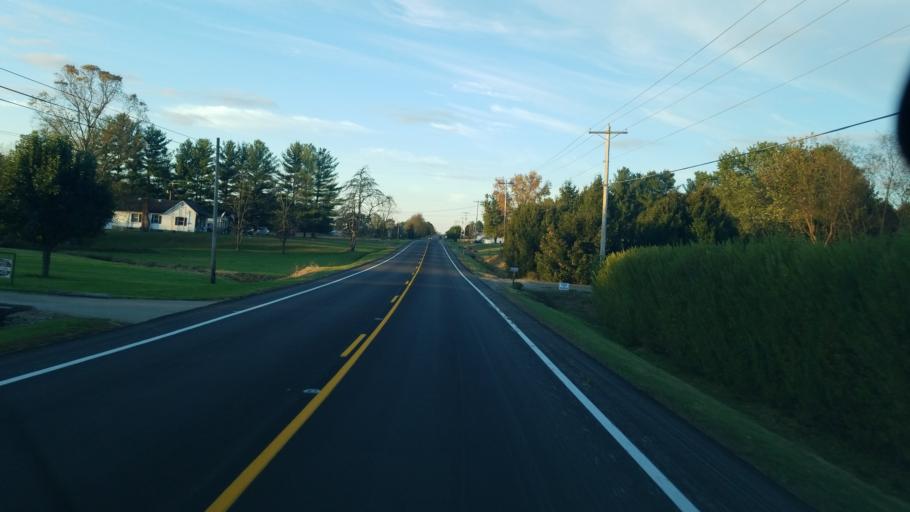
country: US
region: Ohio
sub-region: Jackson County
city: Wellston
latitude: 39.1840
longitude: -82.5101
